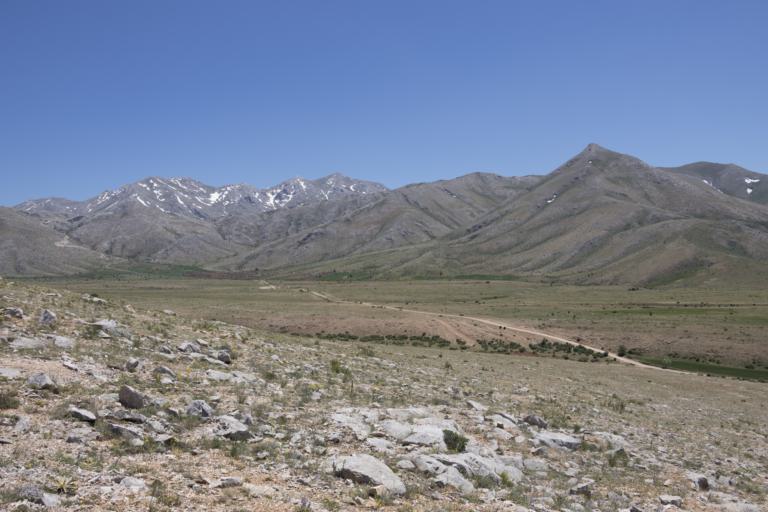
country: TR
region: Kayseri
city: Toklar
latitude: 38.4127
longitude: 36.1020
